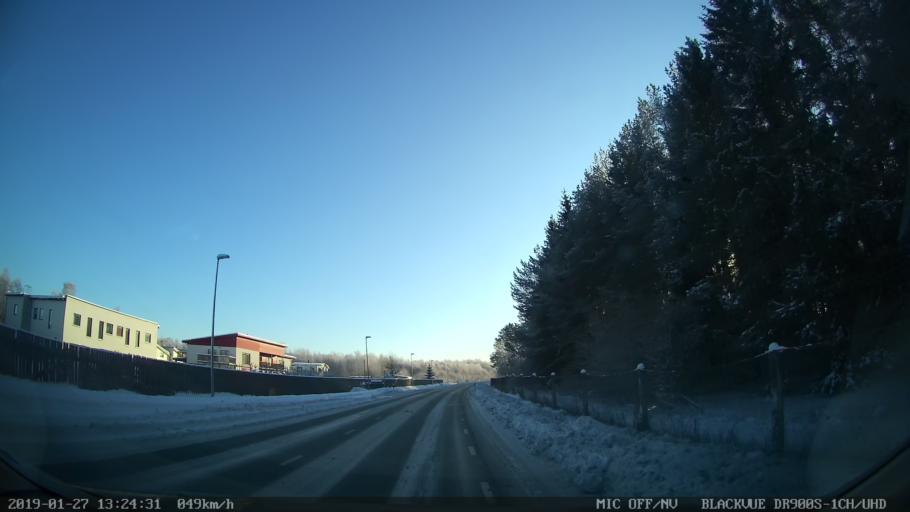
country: EE
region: Harju
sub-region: Tallinna linn
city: Tallinn
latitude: 59.3991
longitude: 24.7918
